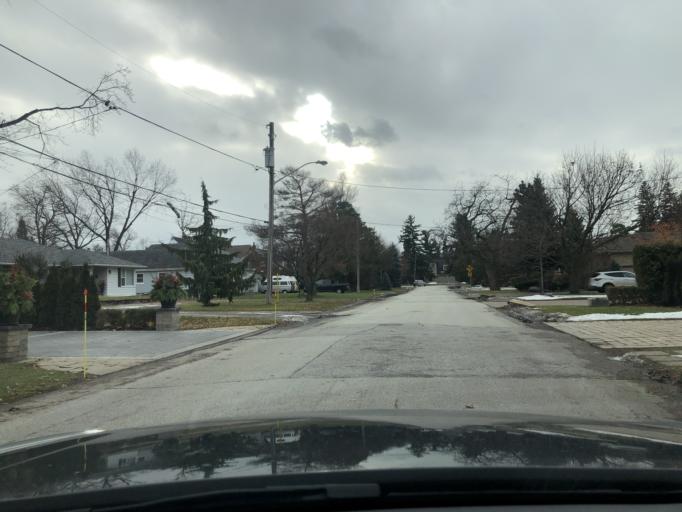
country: CA
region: Ontario
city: Etobicoke
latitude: 43.6959
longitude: -79.5293
